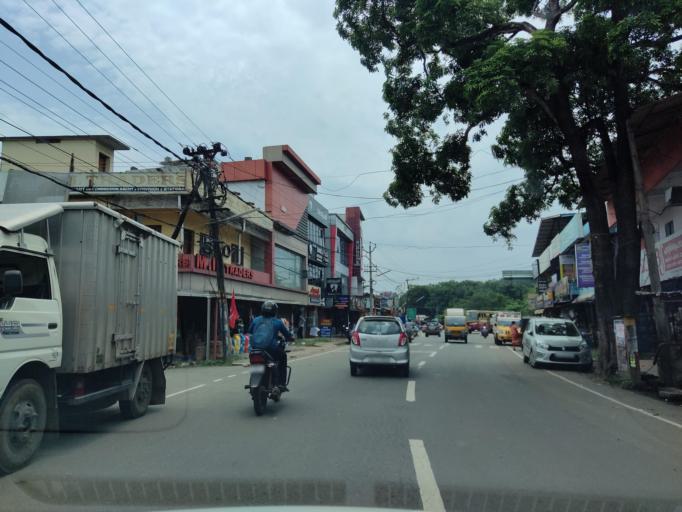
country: IN
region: Kerala
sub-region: Pattanamtitta
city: Adur
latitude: 9.2247
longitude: 76.6753
